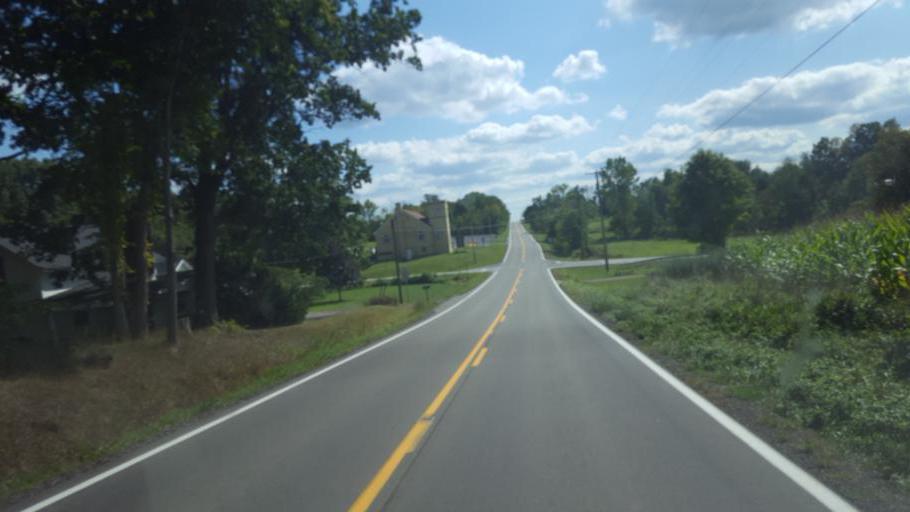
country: US
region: Ohio
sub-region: Ashland County
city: Ashland
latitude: 40.8722
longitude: -82.2117
